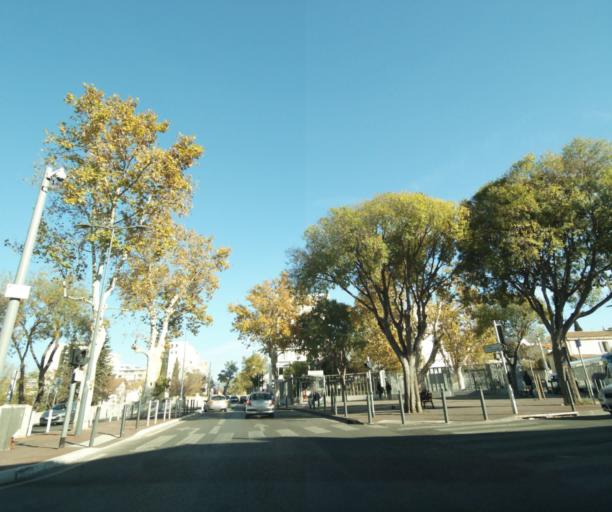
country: FR
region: Provence-Alpes-Cote d'Azur
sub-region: Departement des Bouches-du-Rhone
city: Marseille 11
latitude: 43.2830
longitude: 5.4328
